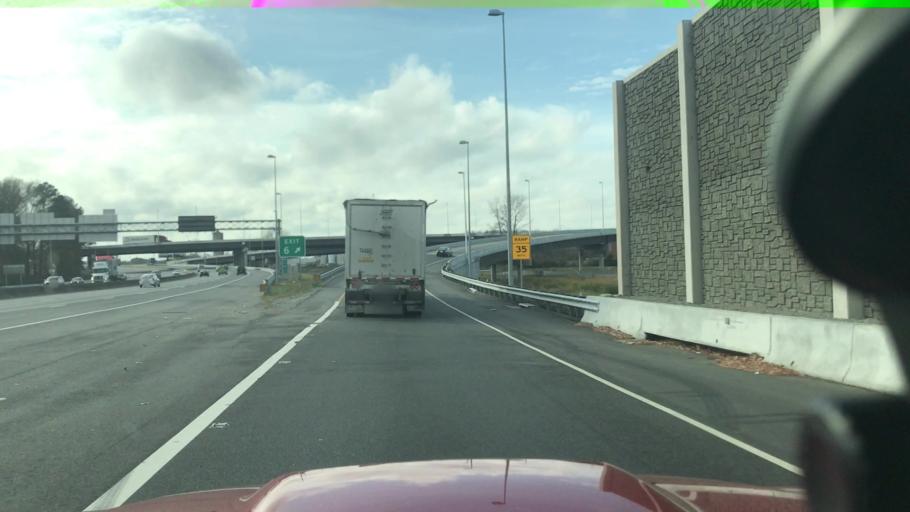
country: US
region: Virginia
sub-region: City of Portsmouth
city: Portsmouth
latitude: 36.8281
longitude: -76.3210
